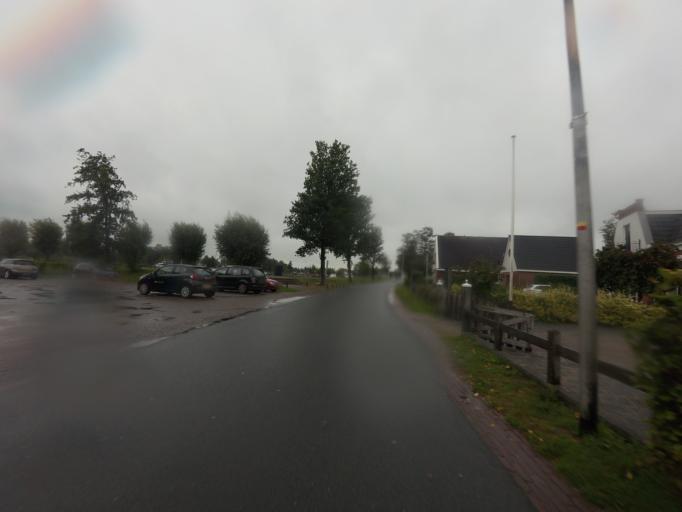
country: NL
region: Friesland
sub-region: Gemeente Tytsjerksteradiel
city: Garyp
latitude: 53.1314
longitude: 5.9412
